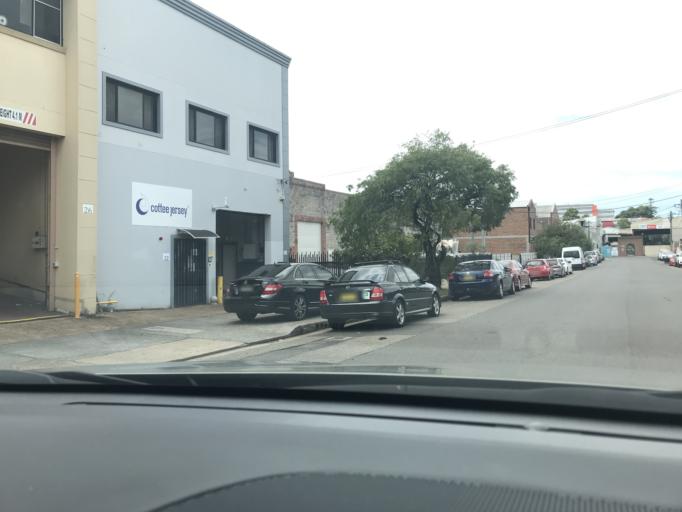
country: AU
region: New South Wales
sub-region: Ashfield
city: Croydon
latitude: -33.8698
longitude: 151.1173
